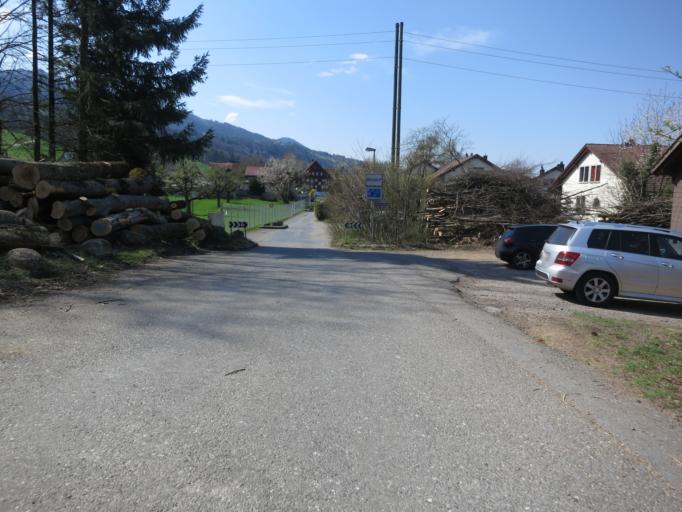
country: CH
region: Schwyz
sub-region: Bezirk March
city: Lachen
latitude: 47.1824
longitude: 8.8556
